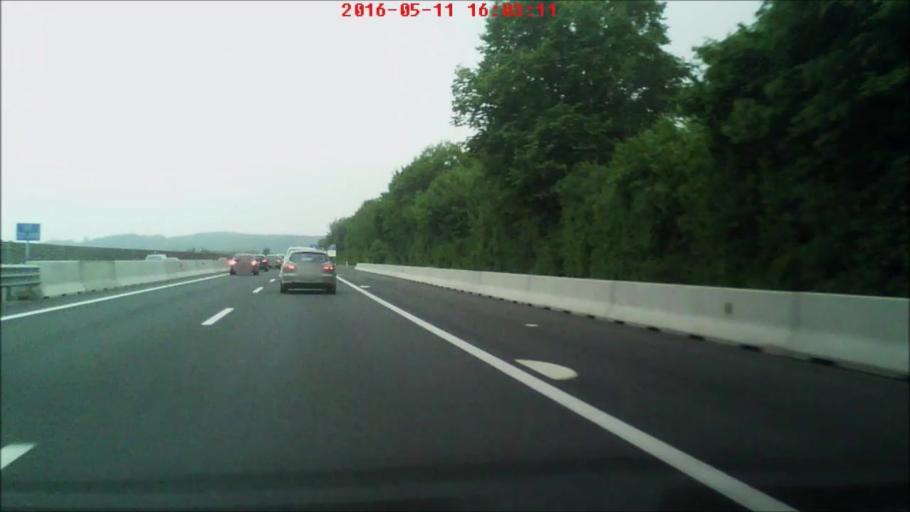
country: AT
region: Styria
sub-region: Politischer Bezirk Leibnitz
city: Weitendorf
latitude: 46.9034
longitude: 15.4722
